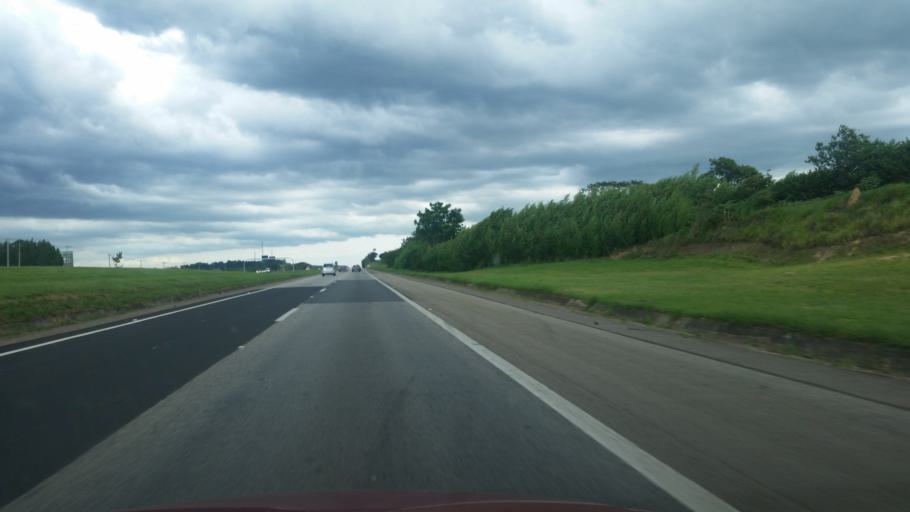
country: BR
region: Sao Paulo
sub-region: Boituva
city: Boituva
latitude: -23.3183
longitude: -47.6252
